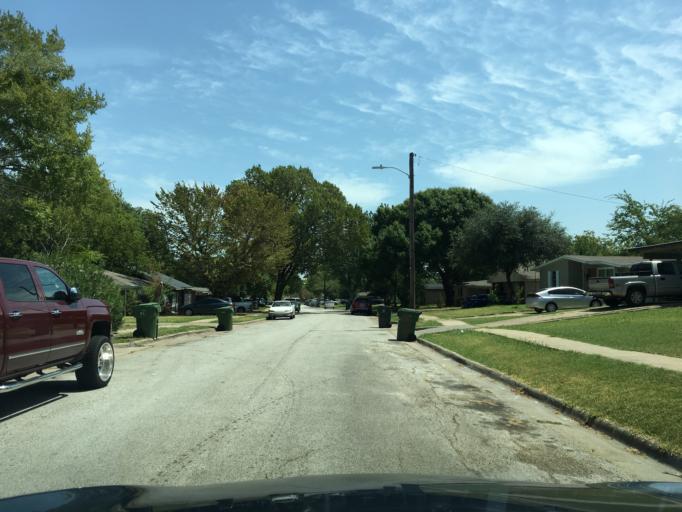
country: US
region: Texas
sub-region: Dallas County
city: Garland
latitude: 32.8951
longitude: -96.6254
